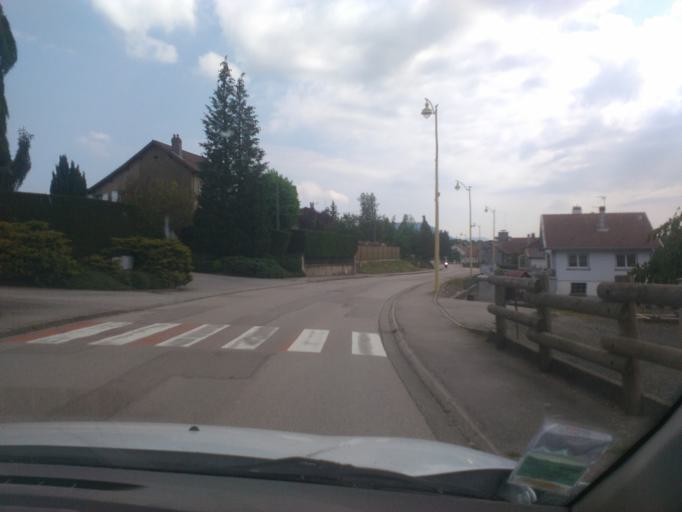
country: FR
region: Lorraine
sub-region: Departement des Vosges
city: Etival-Clairefontaine
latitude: 48.3632
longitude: 6.8566
